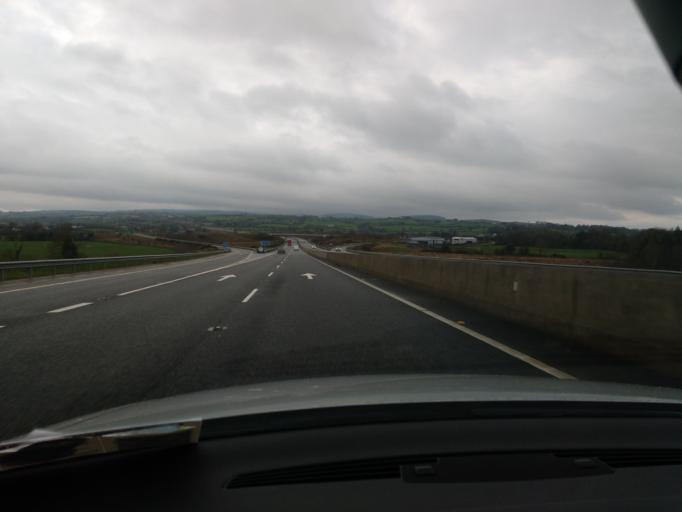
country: IE
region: Munster
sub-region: North Tipperary
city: Nenagh
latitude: 52.8448
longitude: -8.2399
